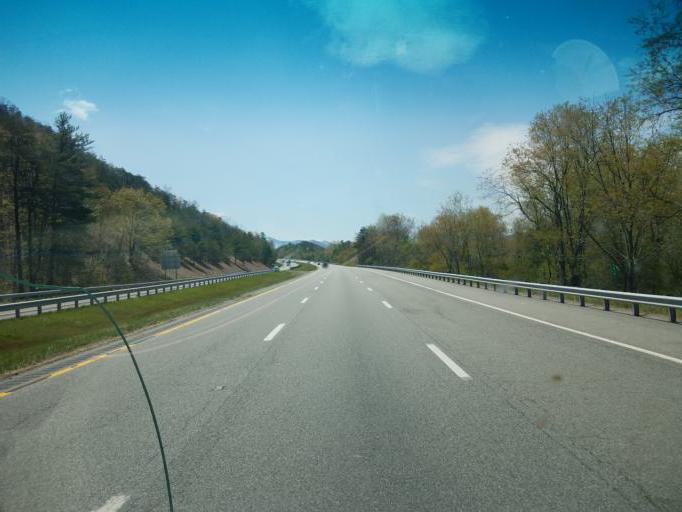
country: US
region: Virginia
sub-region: Bland County
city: Bland
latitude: 37.1730
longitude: -81.1396
